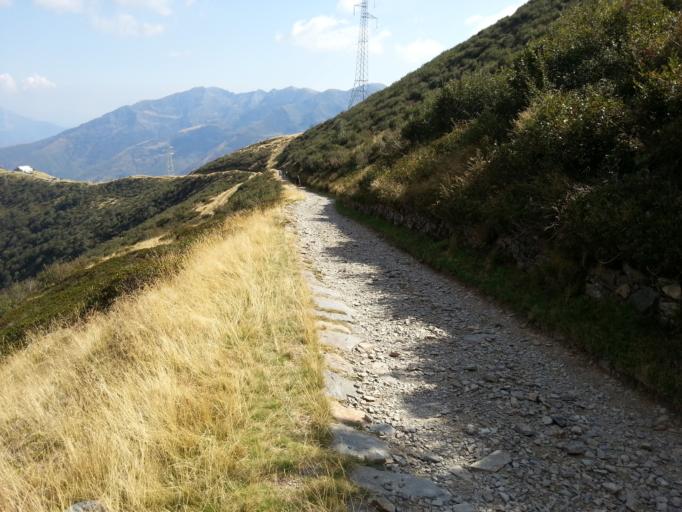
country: IT
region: Lombardy
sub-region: Provincia di Como
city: San Bartolomeo Val Cavargna
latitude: 46.1596
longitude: 9.1652
